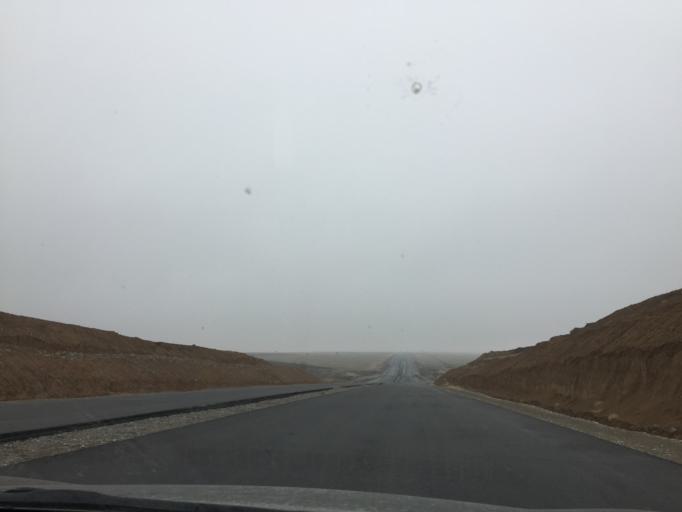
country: KZ
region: Ongtustik Qazaqstan
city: Turar Ryskulov
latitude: 42.5081
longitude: 70.4082
